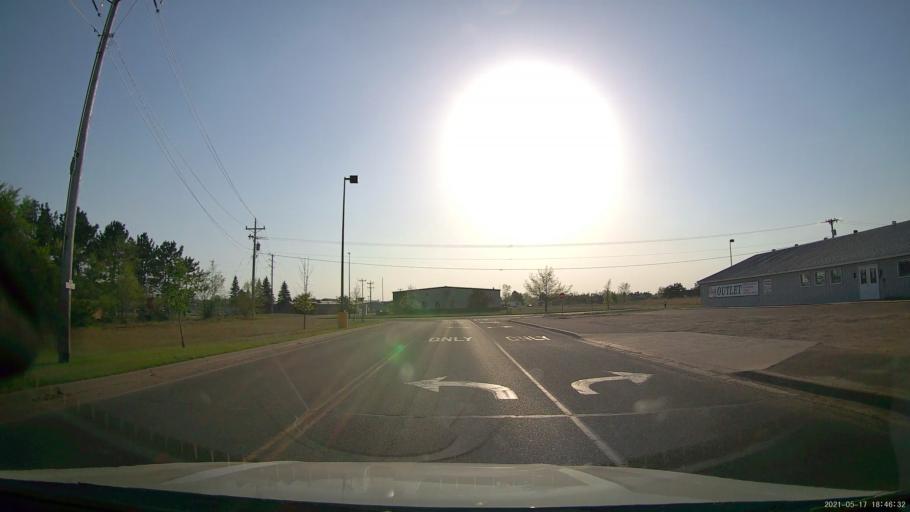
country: US
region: Minnesota
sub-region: Hubbard County
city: Park Rapids
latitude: 46.9247
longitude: -95.0361
